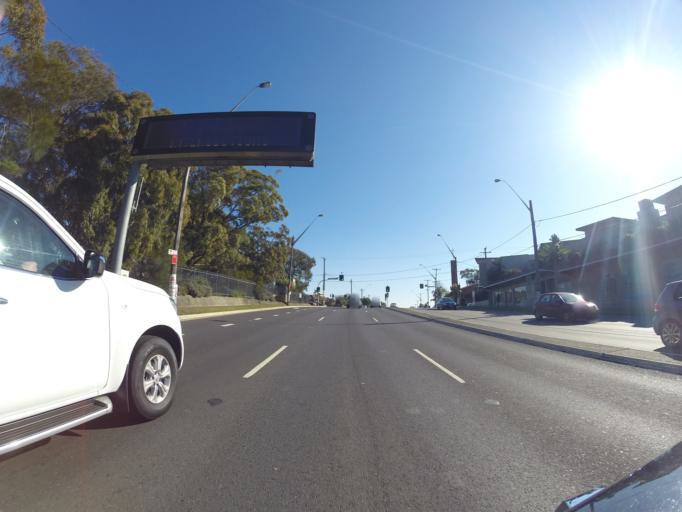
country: AU
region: New South Wales
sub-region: Canterbury
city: Roselands
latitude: -33.9479
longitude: 151.0792
